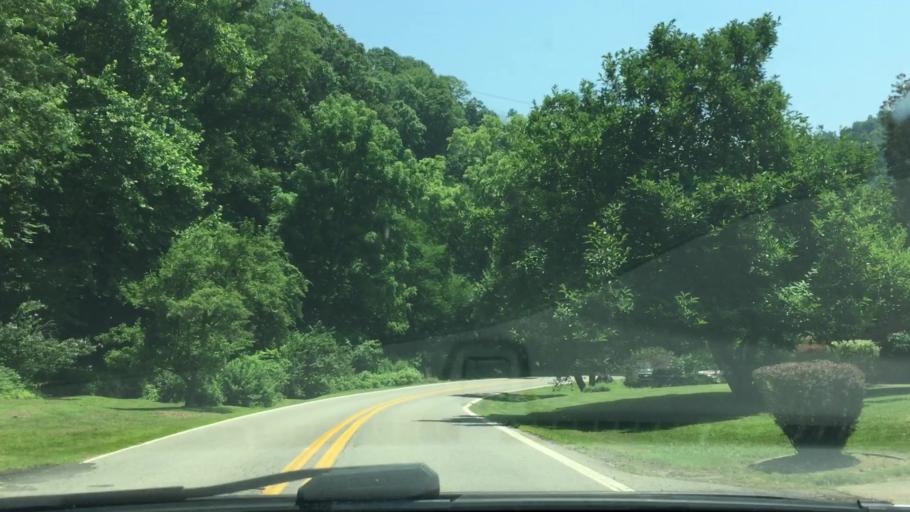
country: US
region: West Virginia
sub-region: Wetzel County
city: New Martinsville
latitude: 39.6963
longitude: -80.8082
